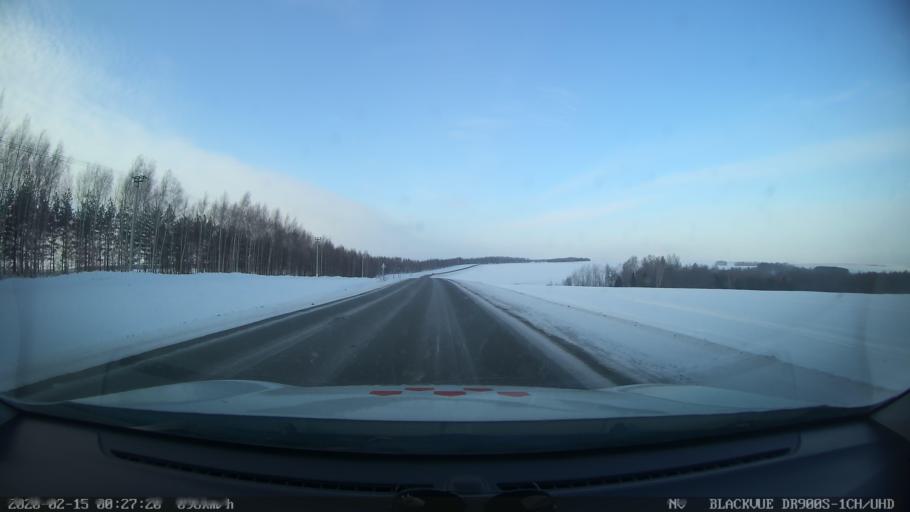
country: RU
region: Tatarstan
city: Verkhniy Uslon
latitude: 55.6267
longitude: 48.8754
